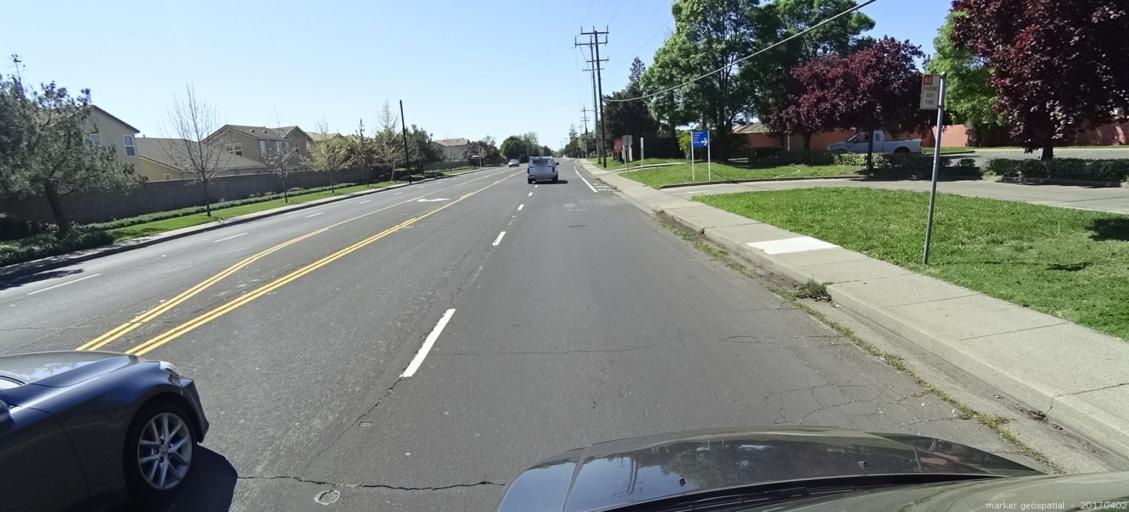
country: US
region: California
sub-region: Sacramento County
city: Parkway
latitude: 38.4822
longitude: -121.4540
